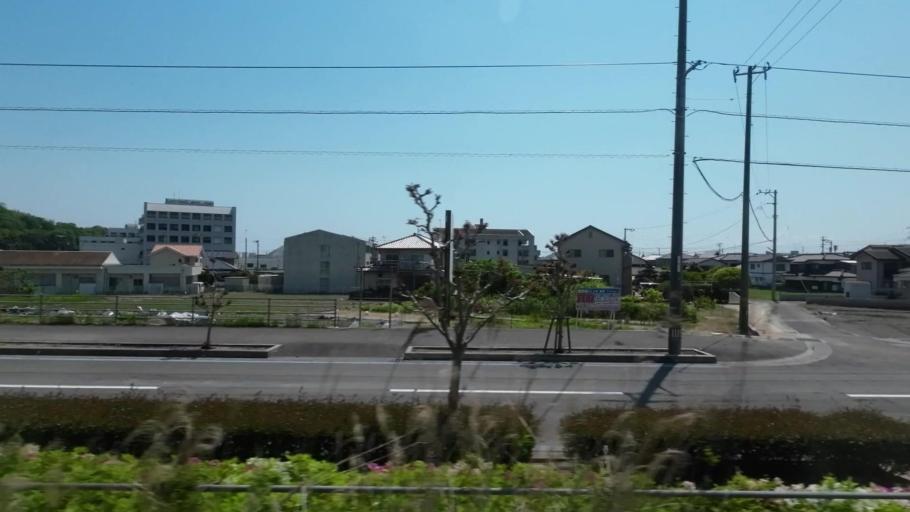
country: JP
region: Ehime
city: Hojo
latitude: 34.0849
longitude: 132.9844
